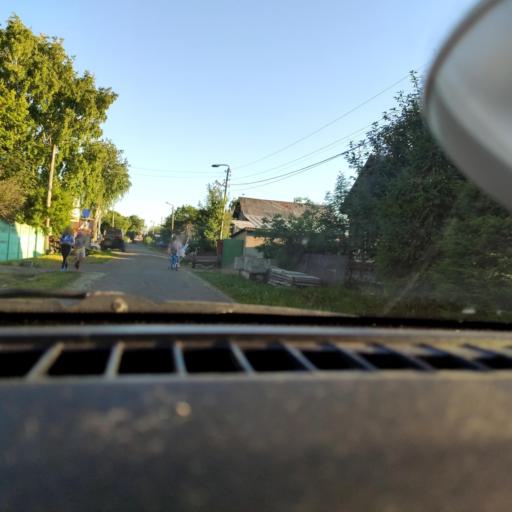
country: RU
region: Perm
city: Froly
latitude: 57.8907
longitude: 56.2560
